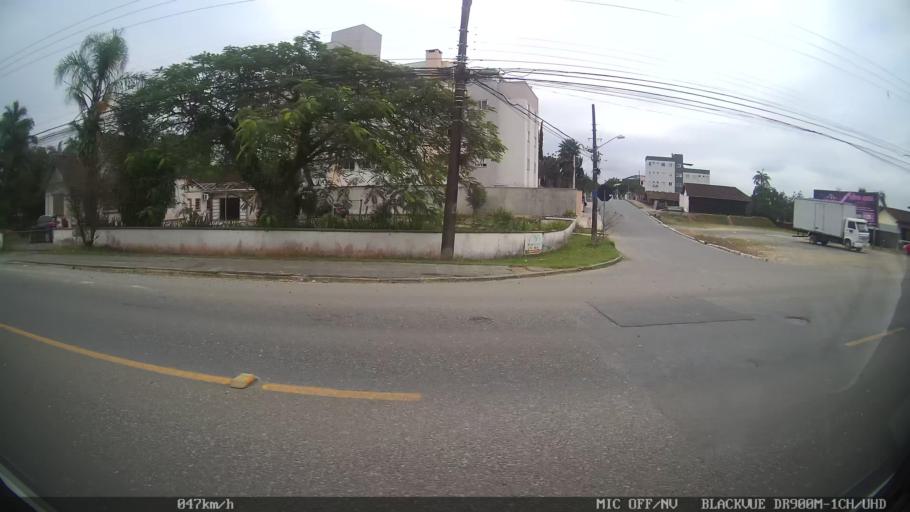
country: BR
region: Santa Catarina
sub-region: Joinville
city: Joinville
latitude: -26.3313
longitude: -48.8731
